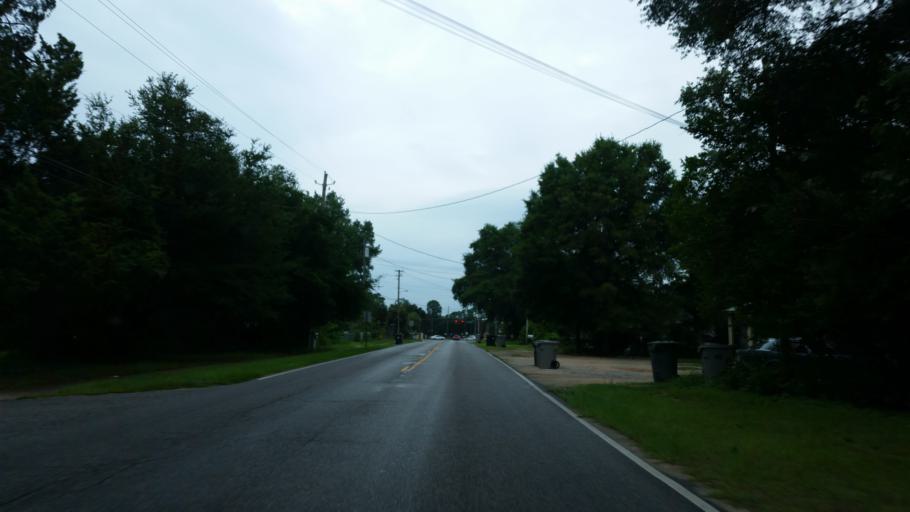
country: US
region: Florida
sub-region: Escambia County
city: Warrington
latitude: 30.3911
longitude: -87.2730
